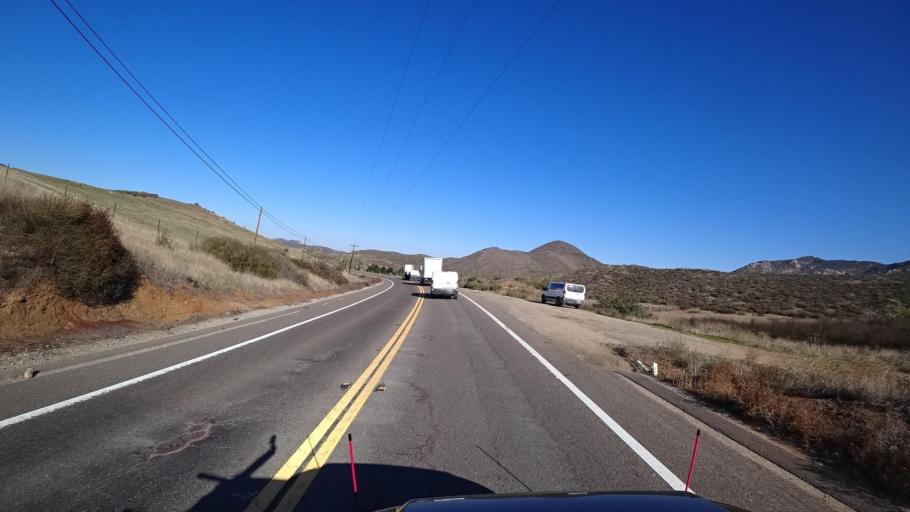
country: US
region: California
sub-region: San Diego County
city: Jamul
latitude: 32.6821
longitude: -116.8409
